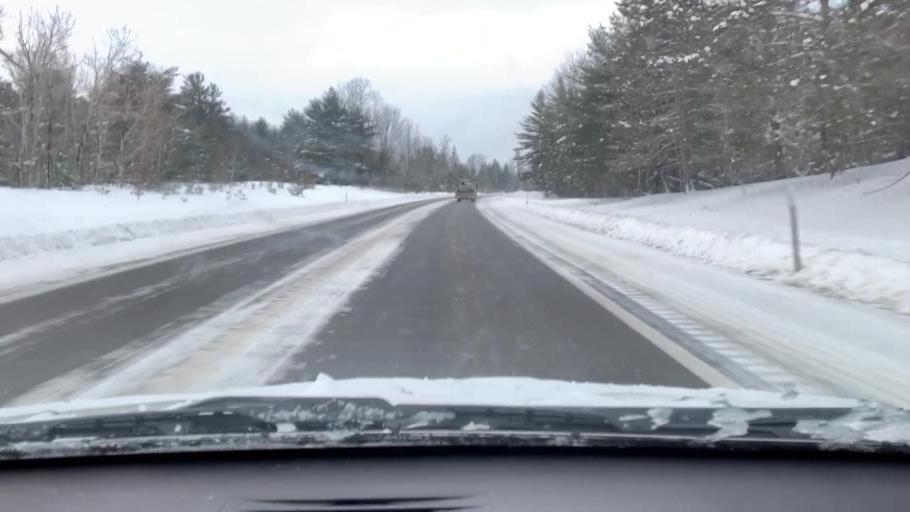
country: US
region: Michigan
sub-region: Kalkaska County
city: Kalkaska
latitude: 44.6491
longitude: -85.2705
